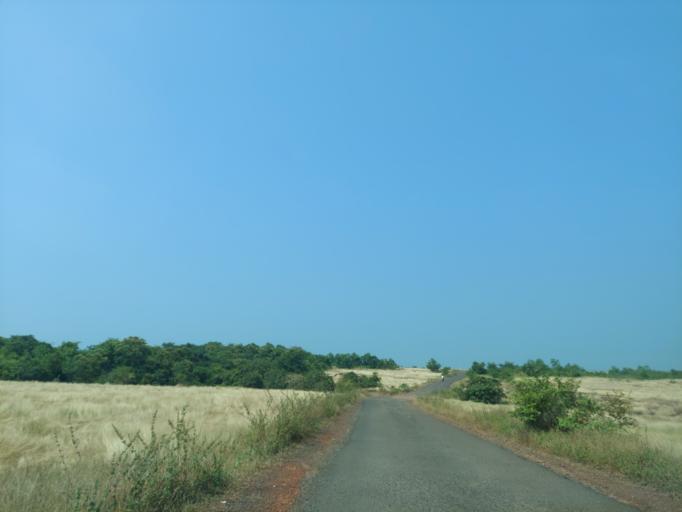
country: IN
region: Maharashtra
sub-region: Sindhudurg
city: Malvan
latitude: 15.9965
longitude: 73.5189
